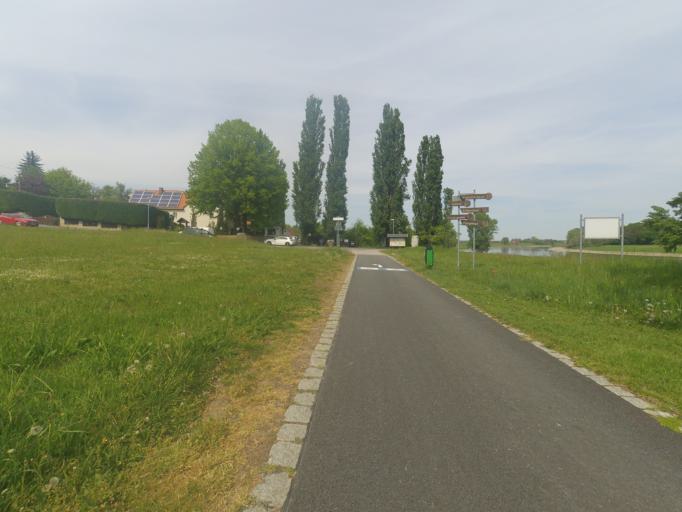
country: DE
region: Saxony
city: Strehla
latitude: 51.3632
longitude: 13.2273
